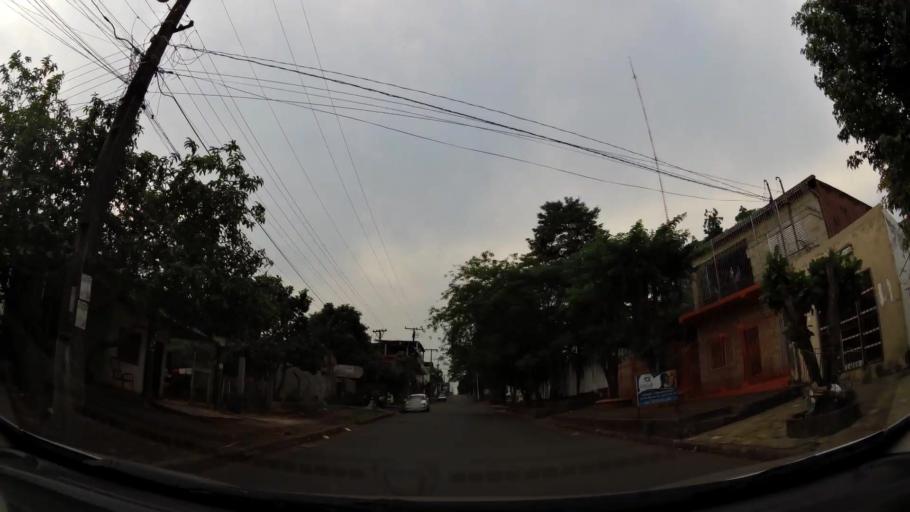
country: PY
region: Alto Parana
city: Presidente Franco
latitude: -25.5391
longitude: -54.6135
